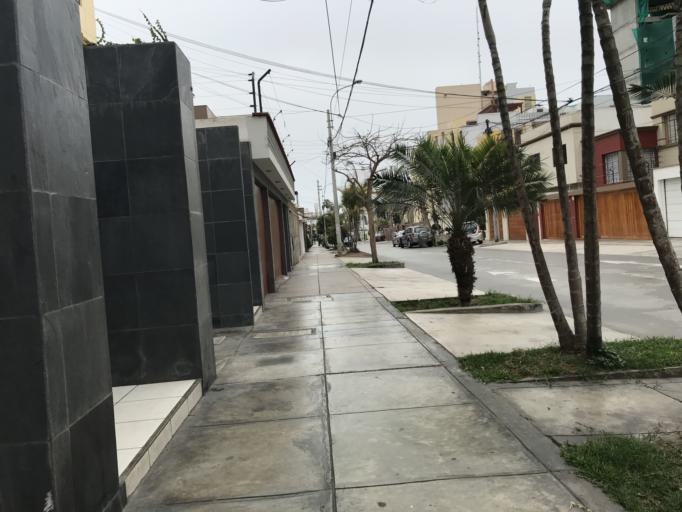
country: PE
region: Lima
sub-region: Lima
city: San Isidro
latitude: -12.0910
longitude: -77.0659
